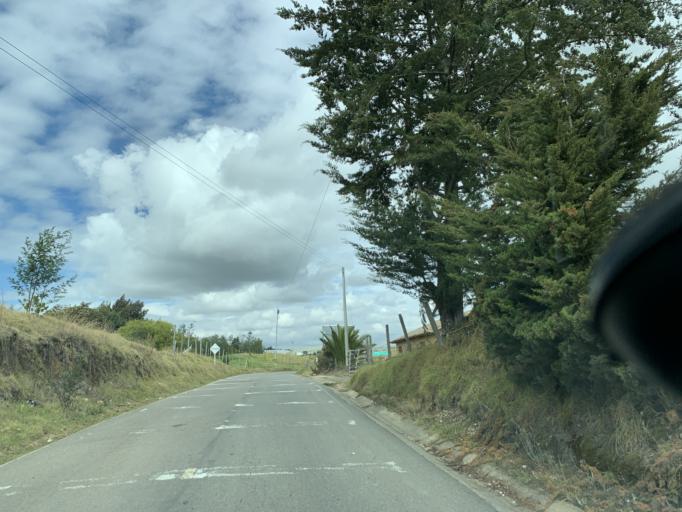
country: CO
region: Boyaca
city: Toca
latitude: 5.5676
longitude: -73.1998
